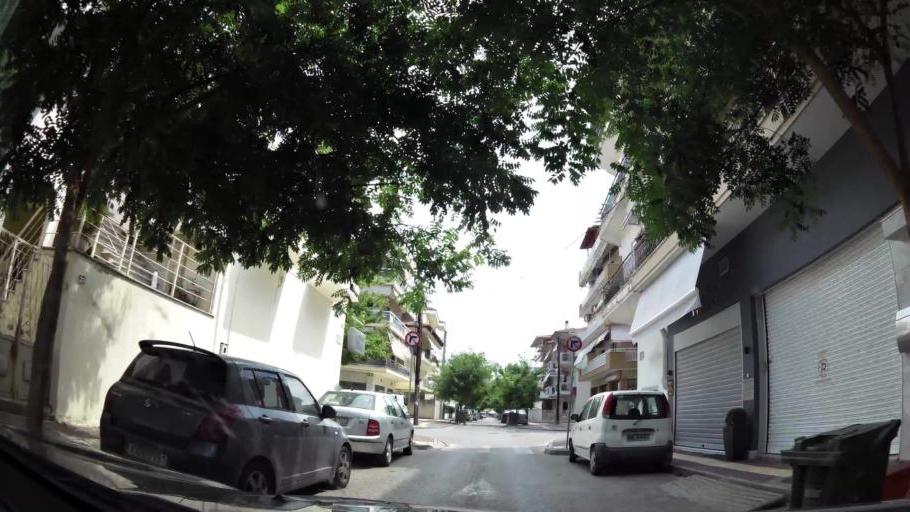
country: GR
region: Central Macedonia
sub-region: Nomos Pierias
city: Katerini
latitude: 40.2733
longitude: 22.5110
